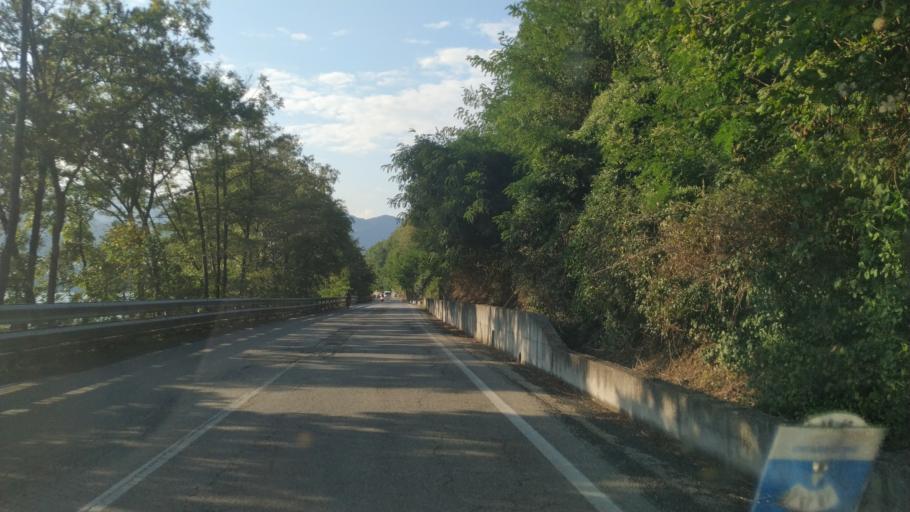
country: IT
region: Piedmont
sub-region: Provincia di Novara
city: Orta San Giulio
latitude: 45.8060
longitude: 8.4171
